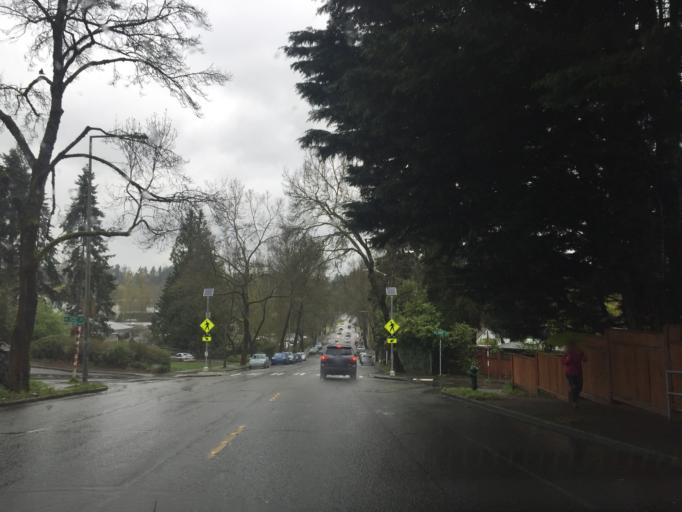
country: US
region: Washington
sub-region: King County
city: Lake Forest Park
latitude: 47.7043
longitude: -122.2909
